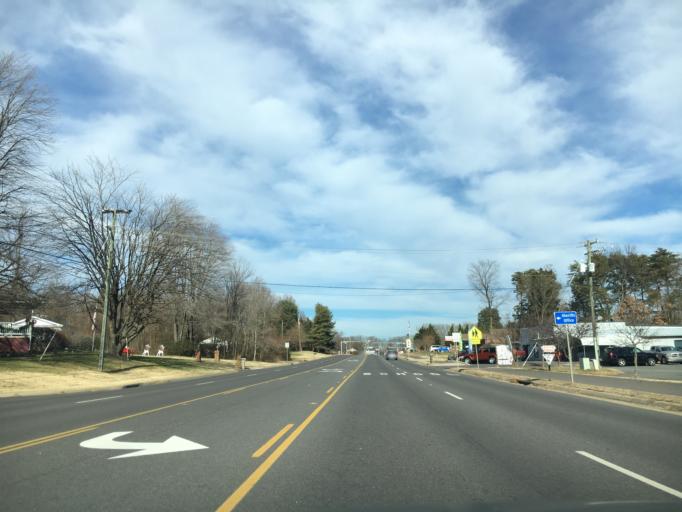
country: US
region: Virginia
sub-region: Culpeper County
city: Culpeper
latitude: 38.4942
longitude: -77.9927
